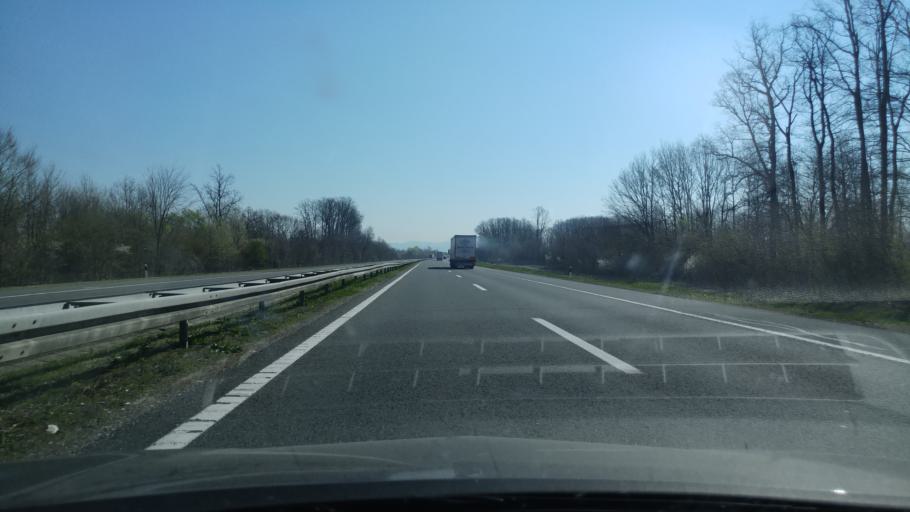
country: HR
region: Brodsko-Posavska
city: Vrbova
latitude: 45.1920
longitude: 17.6101
